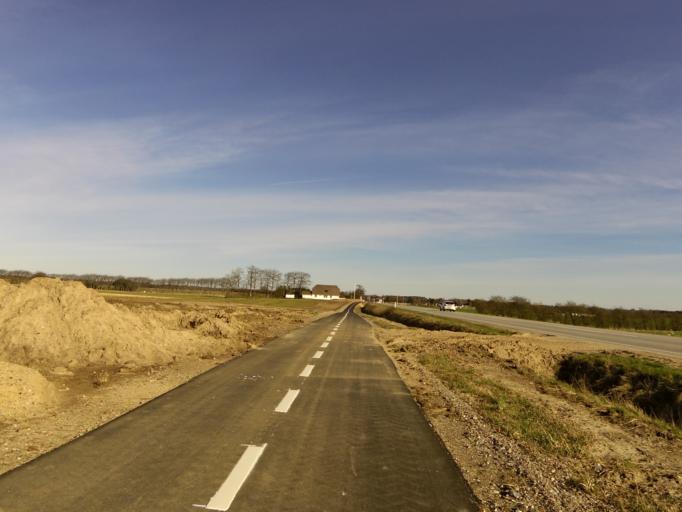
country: DK
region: South Denmark
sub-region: Vejen Kommune
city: Rodding
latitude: 55.3582
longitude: 9.1789
